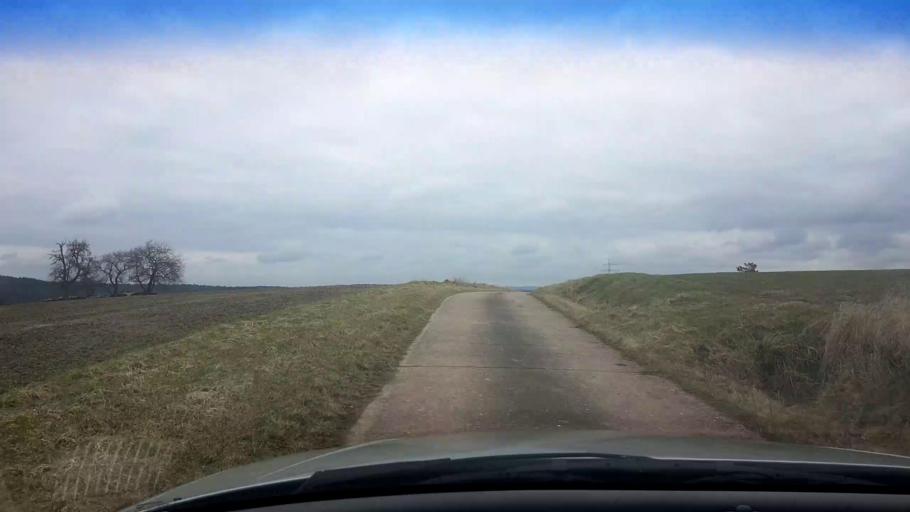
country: DE
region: Bavaria
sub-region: Regierungsbezirk Unterfranken
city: Stettfeld
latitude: 49.9380
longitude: 10.7140
